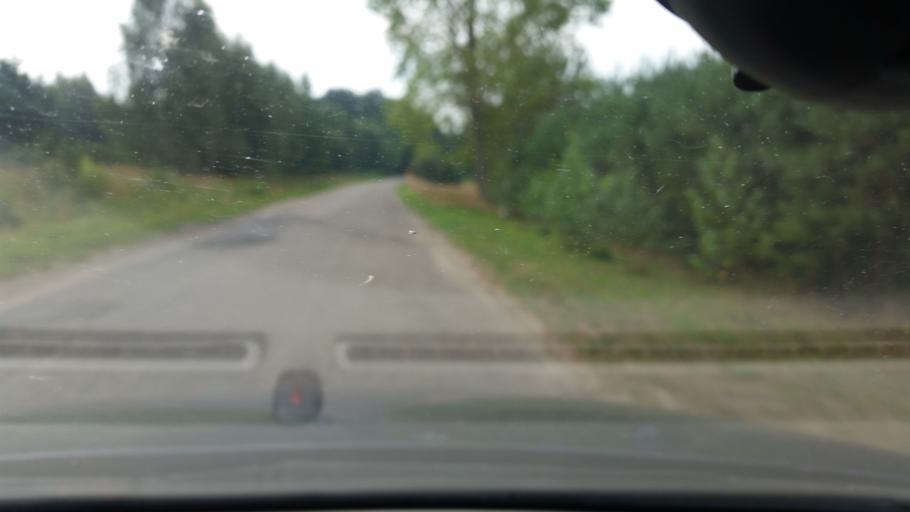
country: PL
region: Pomeranian Voivodeship
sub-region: Powiat wejherowski
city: Choczewo
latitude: 54.7630
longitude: 17.7926
